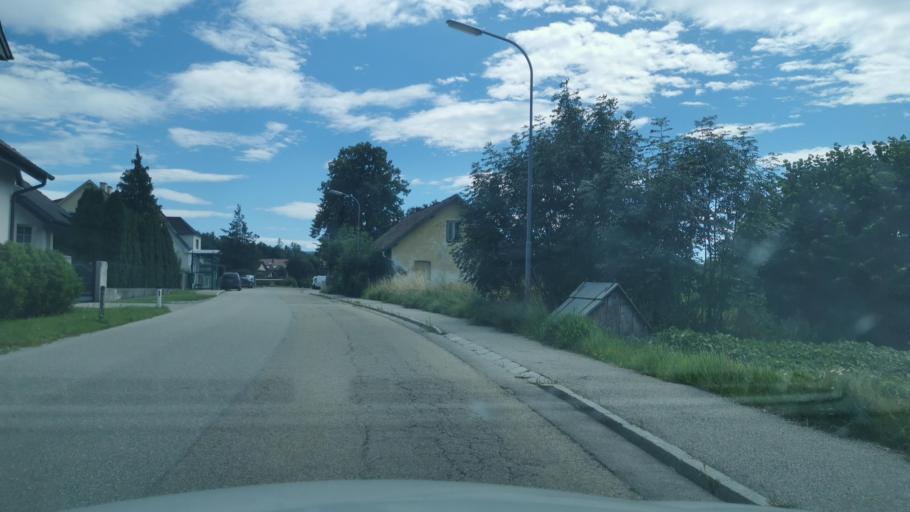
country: AT
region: Lower Austria
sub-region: Sankt Polten Stadt
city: Sankt Poelten
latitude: 48.1564
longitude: 15.6400
